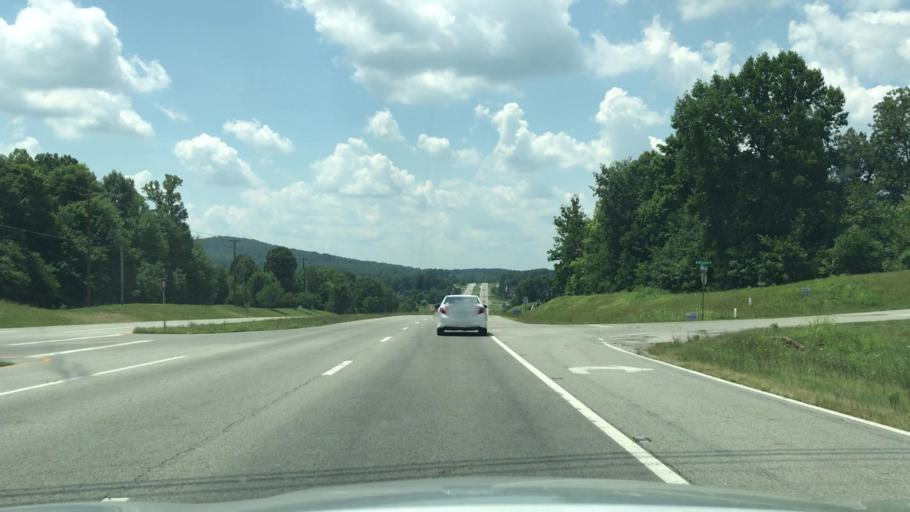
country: US
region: Tennessee
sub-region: Overton County
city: Livingston
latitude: 36.3393
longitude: -85.3498
